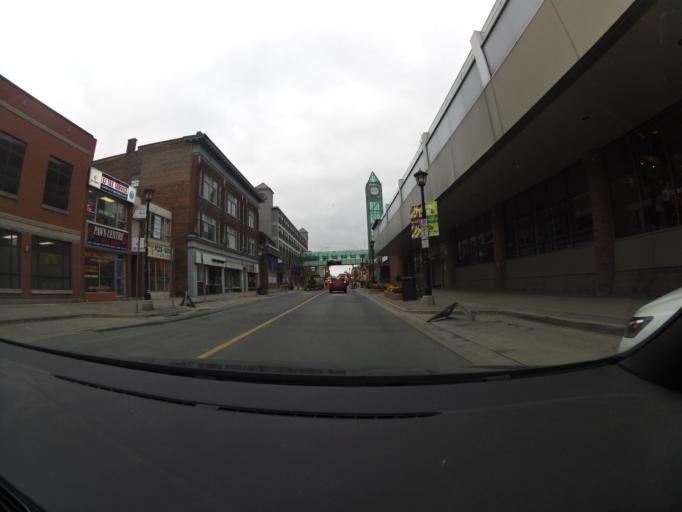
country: CA
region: Ontario
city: Kitchener
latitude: 43.4486
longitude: -80.4863
